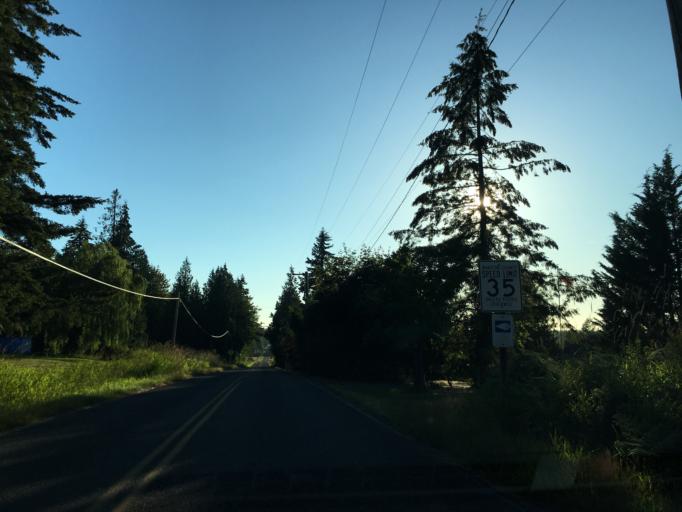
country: US
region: Washington
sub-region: Whatcom County
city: Sudden Valley
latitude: 48.8181
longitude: -122.3276
